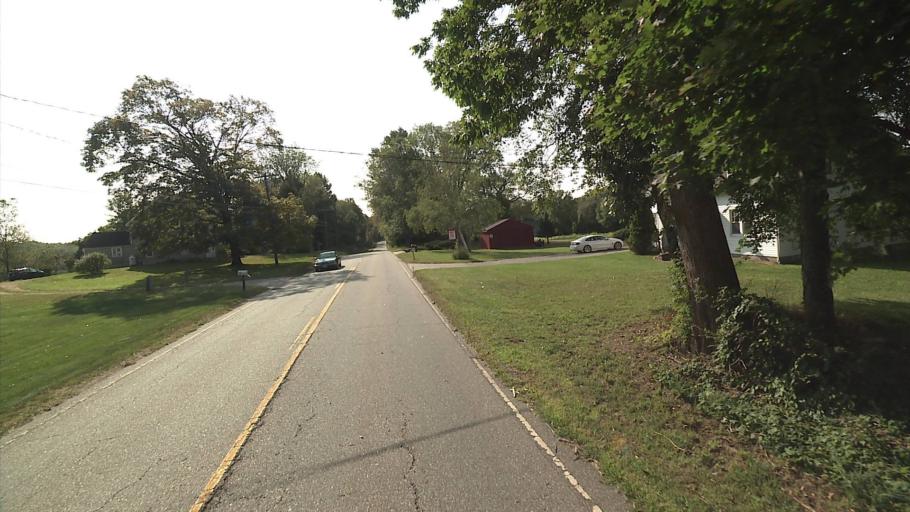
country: US
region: Connecticut
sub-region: Windham County
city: Willimantic
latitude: 41.6610
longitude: -72.2506
